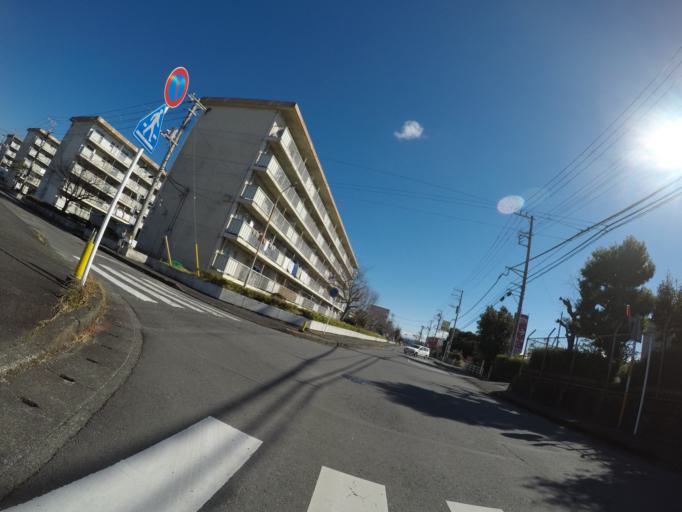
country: JP
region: Shizuoka
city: Numazu
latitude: 35.1280
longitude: 138.8056
